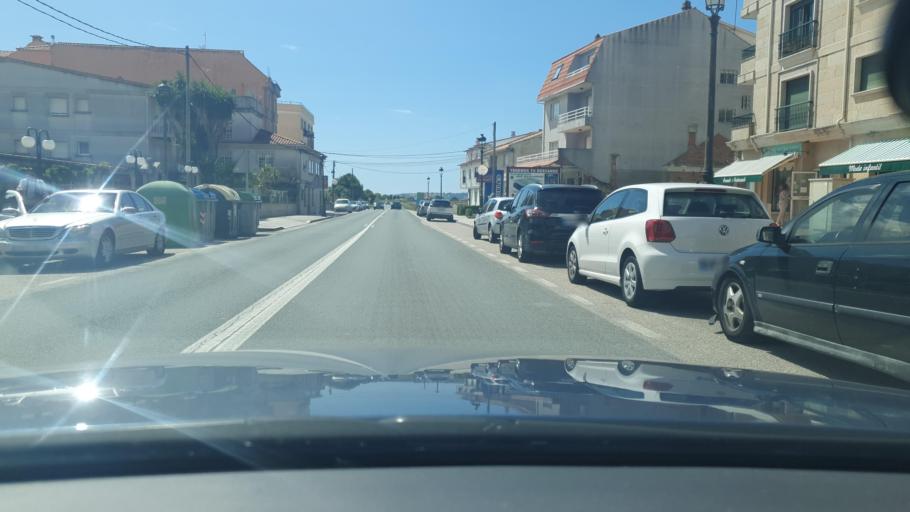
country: ES
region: Galicia
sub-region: Provincia de Pontevedra
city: O Grove
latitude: 42.4468
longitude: -8.8643
